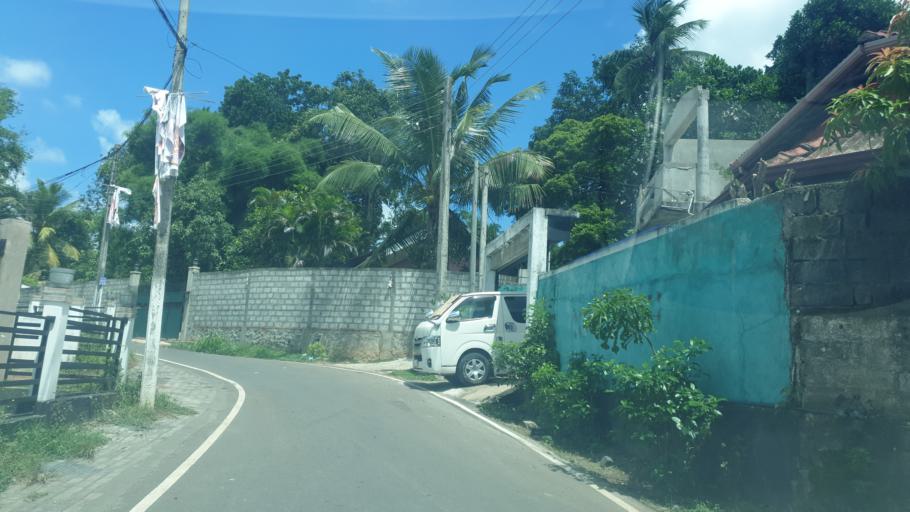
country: LK
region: Western
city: Kandana
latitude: 7.0554
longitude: 79.9287
